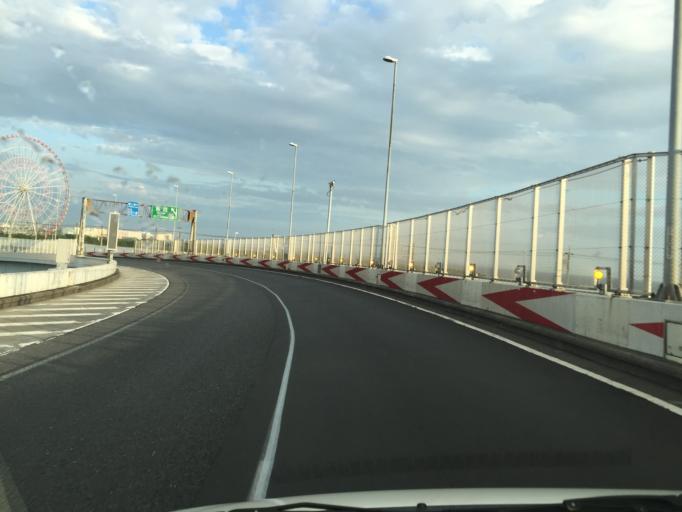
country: JP
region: Tokyo
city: Urayasu
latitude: 35.6477
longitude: 139.8509
